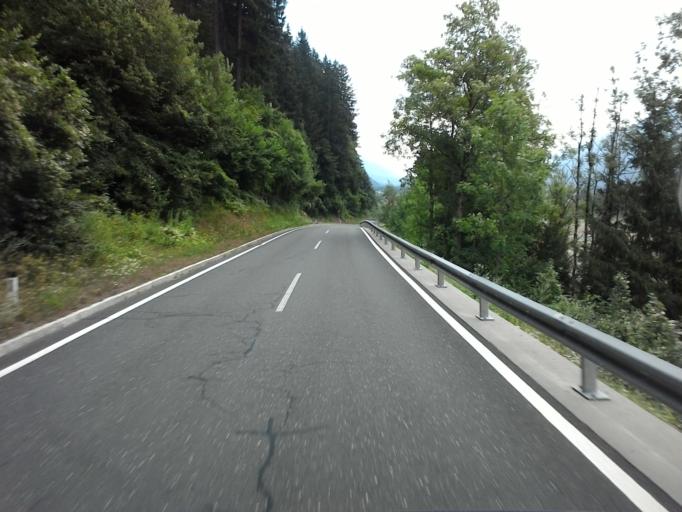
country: AT
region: Carinthia
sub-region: Politischer Bezirk Spittal an der Drau
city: Oberdrauburg
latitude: 46.6700
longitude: 12.9800
